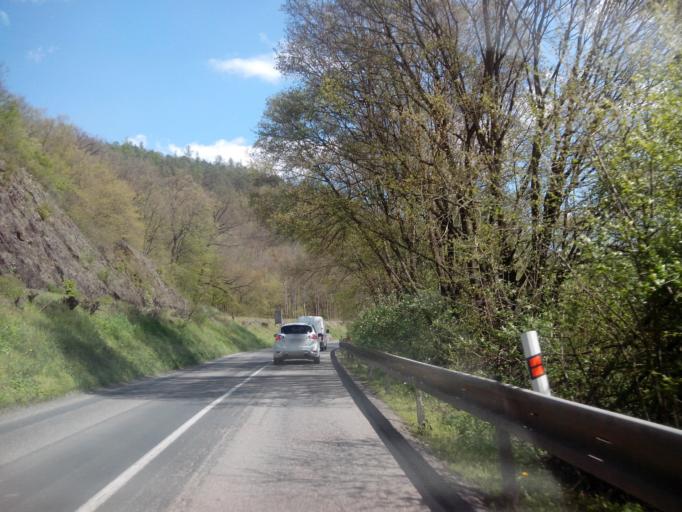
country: CZ
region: Central Bohemia
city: Nizbor
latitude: 49.9997
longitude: 14.0157
